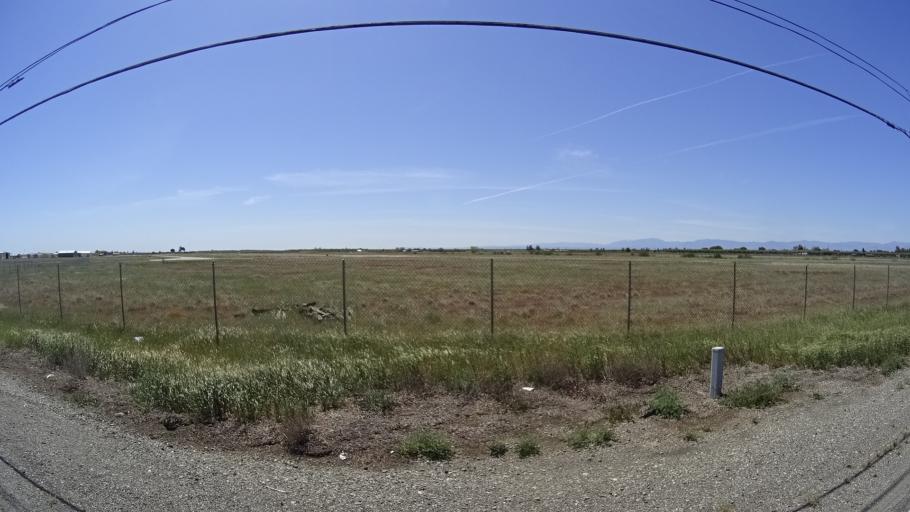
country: US
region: California
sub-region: Glenn County
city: Orland
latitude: 39.7277
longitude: -122.1475
